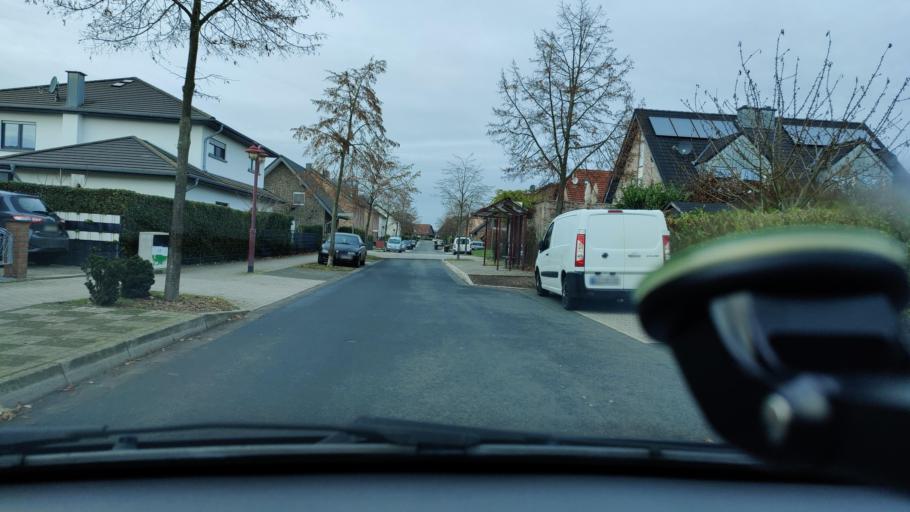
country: DE
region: North Rhine-Westphalia
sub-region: Regierungsbezirk Dusseldorf
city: Xanten
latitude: 51.6620
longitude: 6.4683
